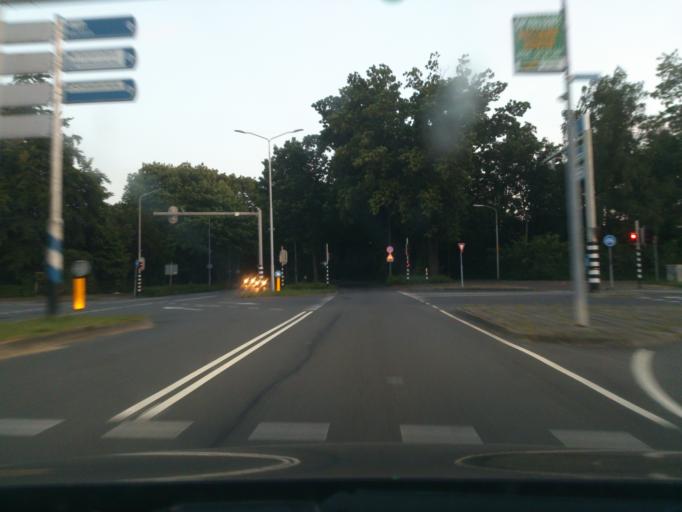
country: NL
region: Gelderland
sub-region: Gemeente Nijmegen
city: Nijmegen
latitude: 51.8164
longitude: 5.8279
